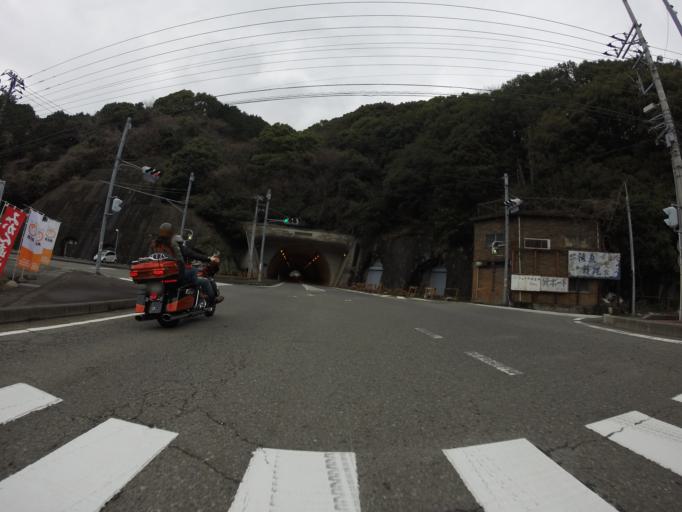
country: JP
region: Shizuoka
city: Numazu
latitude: 35.0188
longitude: 138.8849
